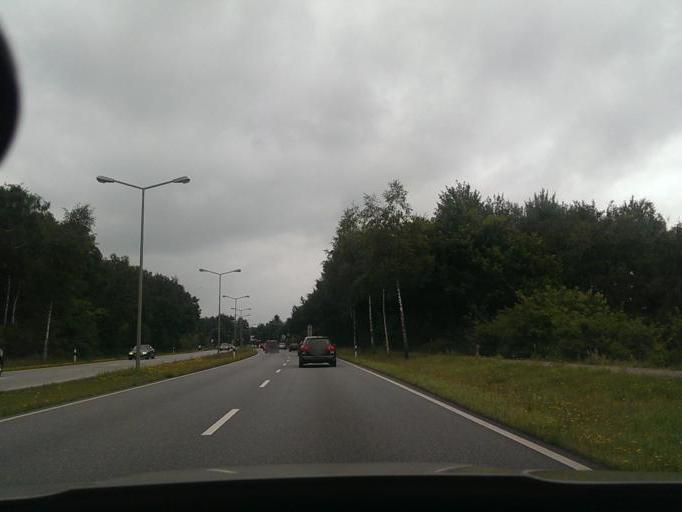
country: DE
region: Hamburg
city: Langenhorn
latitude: 53.6455
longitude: 9.9697
